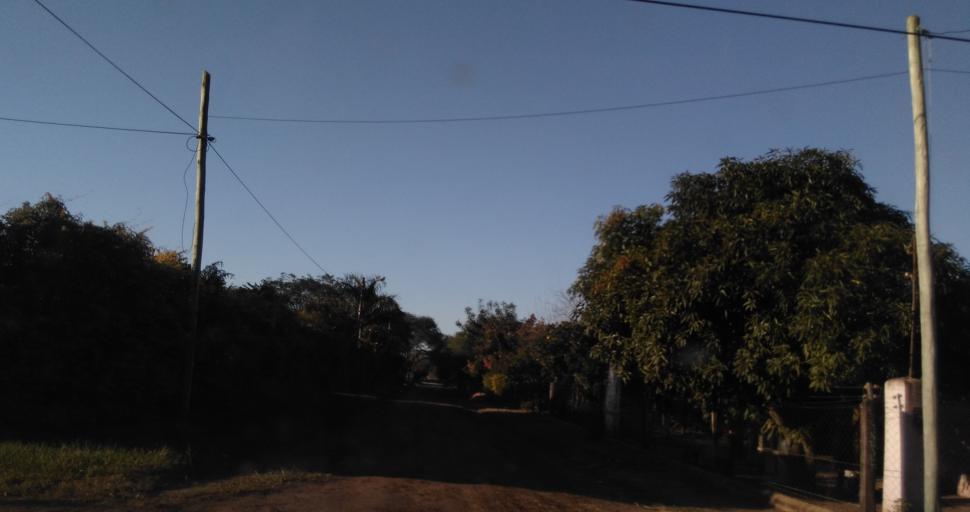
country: AR
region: Chaco
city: Colonia Benitez
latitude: -27.3282
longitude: -58.9550
